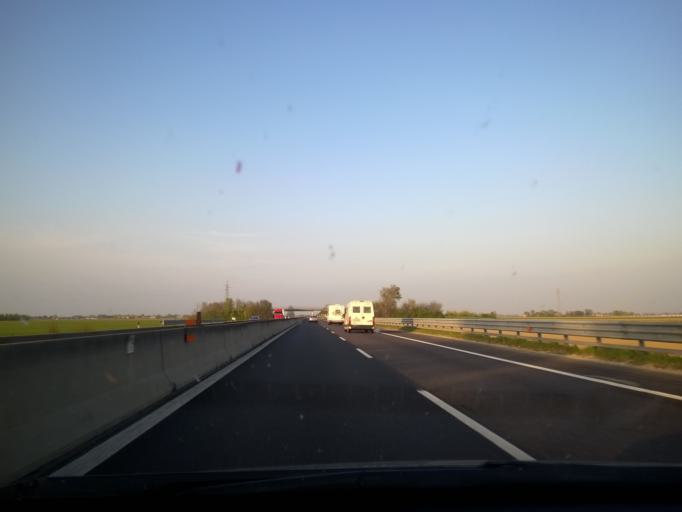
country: IT
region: Veneto
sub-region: Provincia di Rovigo
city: Fiesso Umbertiano
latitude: 44.9449
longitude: 11.6305
